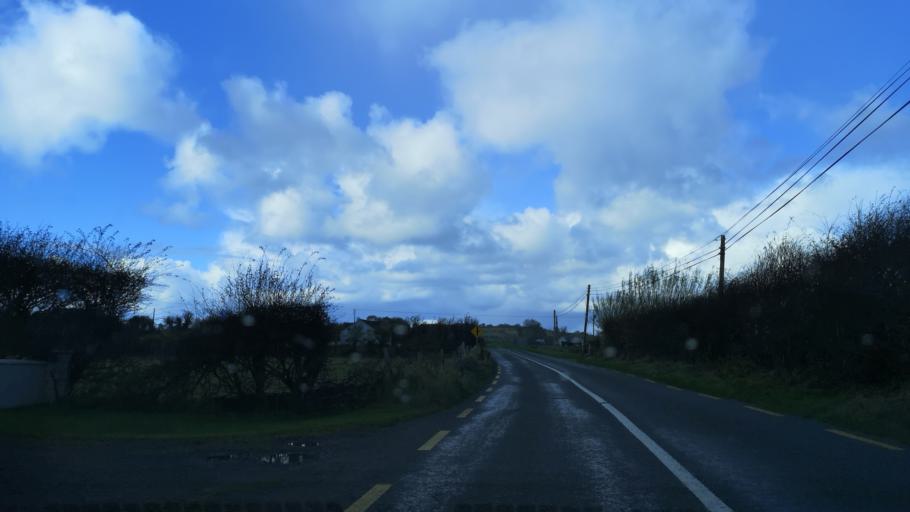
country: IE
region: Connaught
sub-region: Maigh Eo
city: Westport
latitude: 53.7796
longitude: -9.4350
